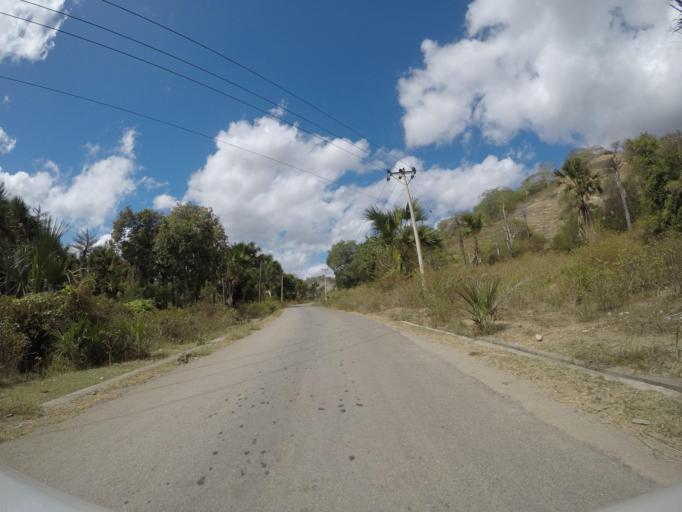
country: TL
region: Lautem
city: Lospalos
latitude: -8.4141
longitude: 126.8264
